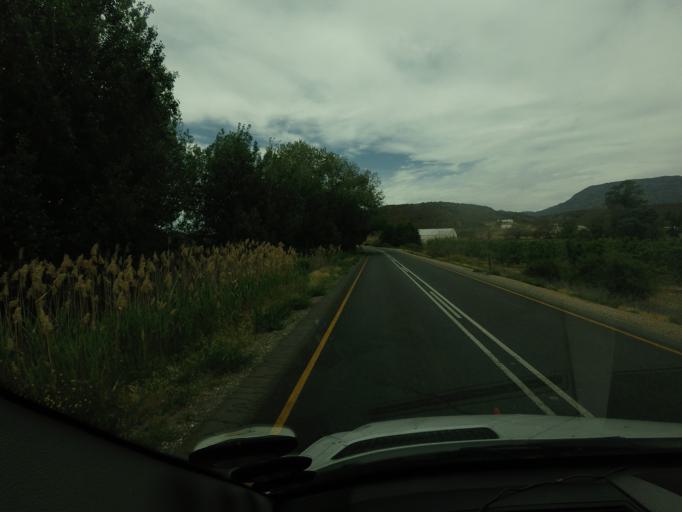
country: ZA
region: Western Cape
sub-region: Overberg District Municipality
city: Swellendam
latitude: -33.8560
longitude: 20.7991
